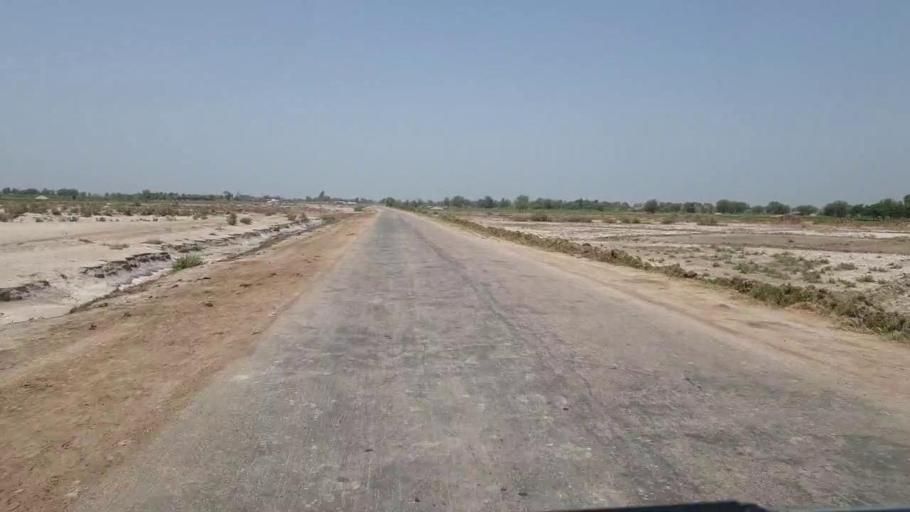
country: PK
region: Sindh
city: Nawabshah
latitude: 26.3615
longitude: 68.4060
